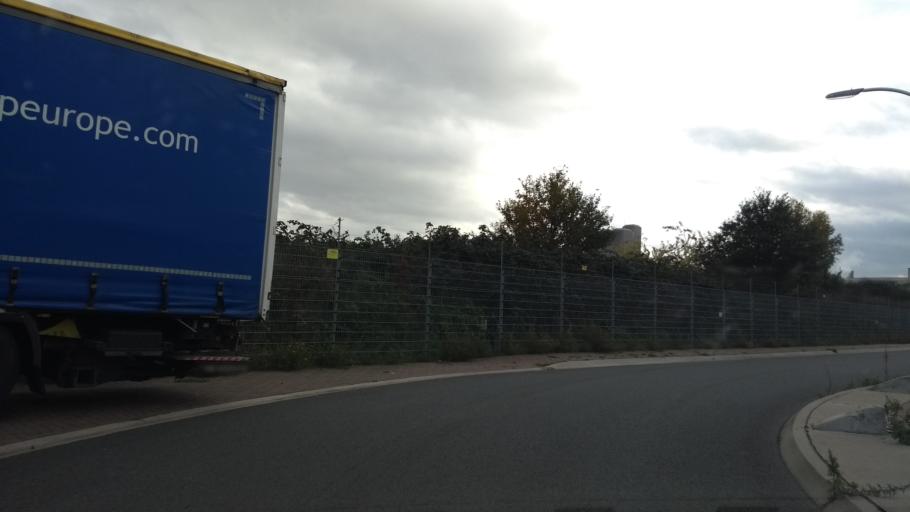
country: NL
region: Overijssel
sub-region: Gemeente Hengelo
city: Hengelo
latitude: 52.2493
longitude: 6.7946
